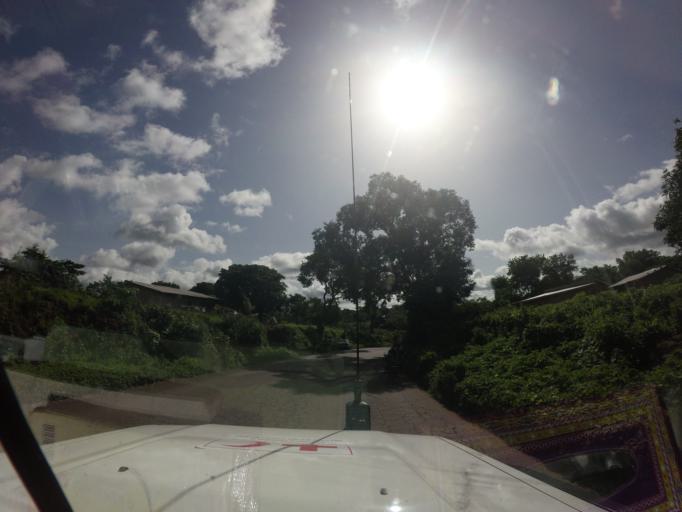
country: GN
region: Mamou
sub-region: Mamou Prefecture
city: Mamou
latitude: 10.3058
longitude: -12.2954
